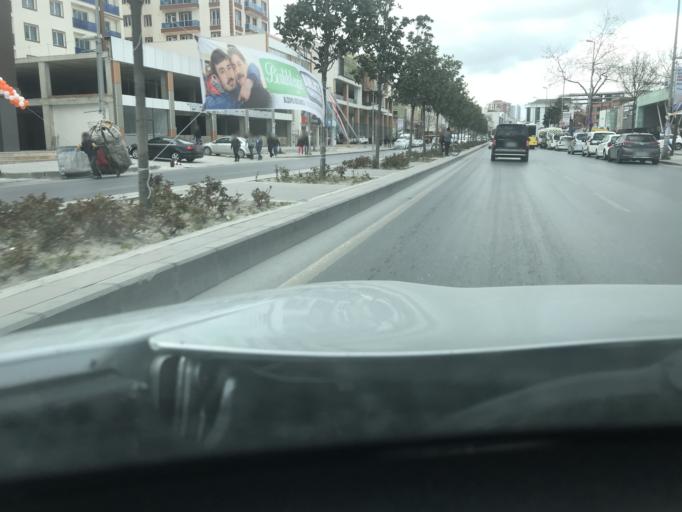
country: TR
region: Istanbul
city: Esenyurt
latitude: 41.0399
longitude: 28.6775
